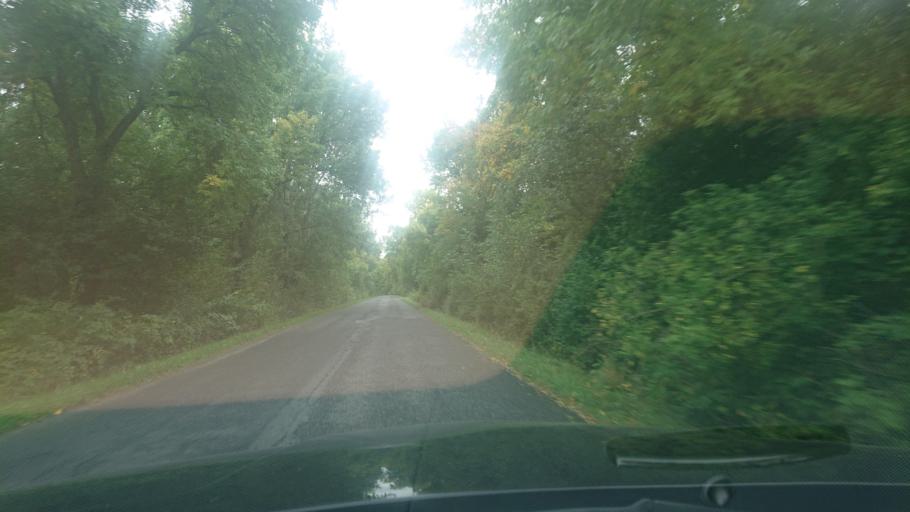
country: PL
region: Lower Silesian Voivodeship
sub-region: Powiat klodzki
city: Miedzylesie
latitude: 50.2261
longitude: 16.7268
